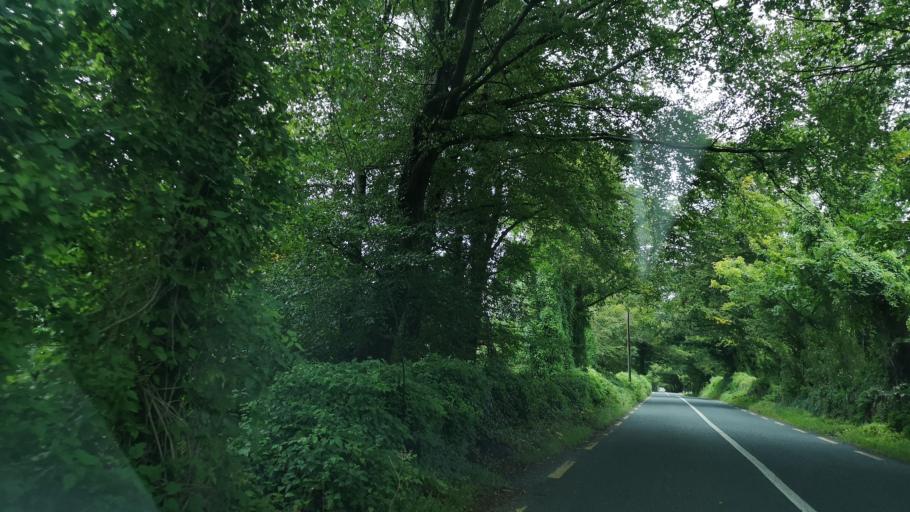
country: IE
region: Connaught
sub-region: County Galway
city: Athenry
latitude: 53.3322
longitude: -8.7688
